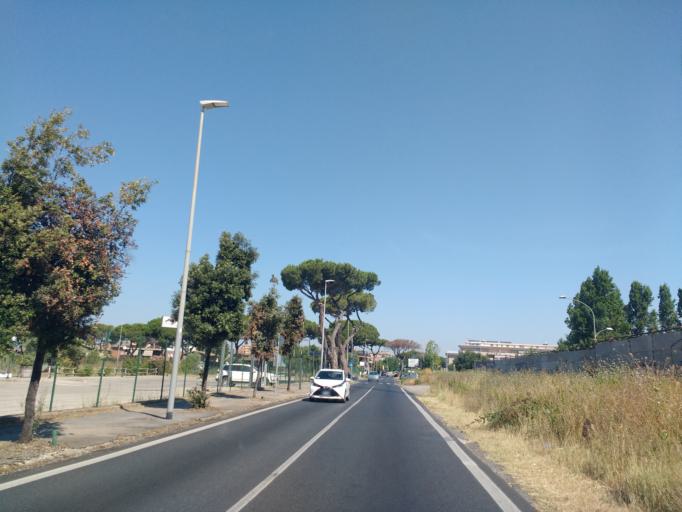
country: IT
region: Latium
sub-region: Citta metropolitana di Roma Capitale
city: Vitinia
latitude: 41.7727
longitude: 12.3719
